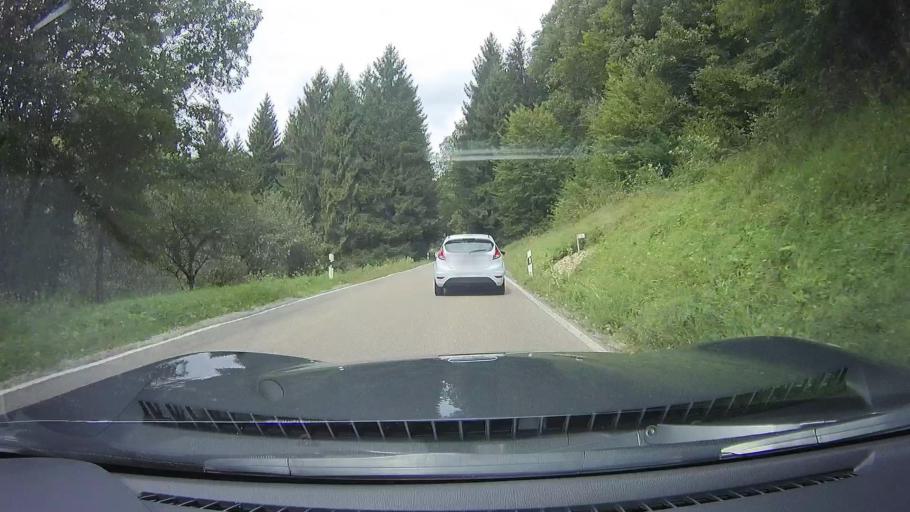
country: DE
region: Baden-Wuerttemberg
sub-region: Regierungsbezirk Stuttgart
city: Althutte
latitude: 48.9008
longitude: 9.5763
